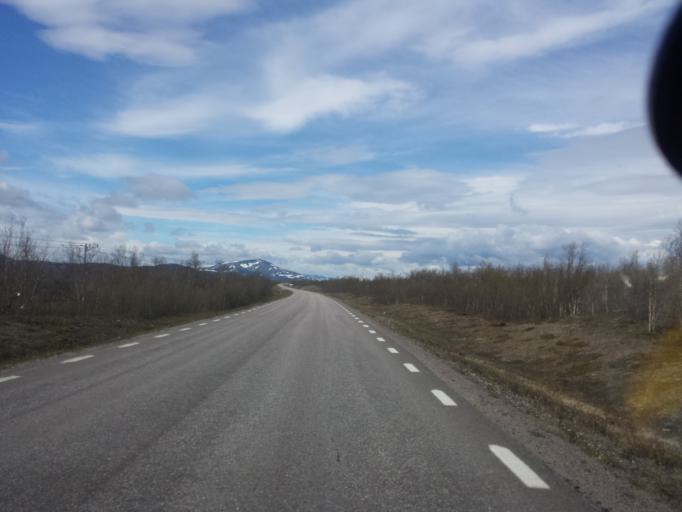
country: SE
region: Norrbotten
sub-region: Kiruna Kommun
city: Kiruna
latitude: 68.0520
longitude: 19.8299
